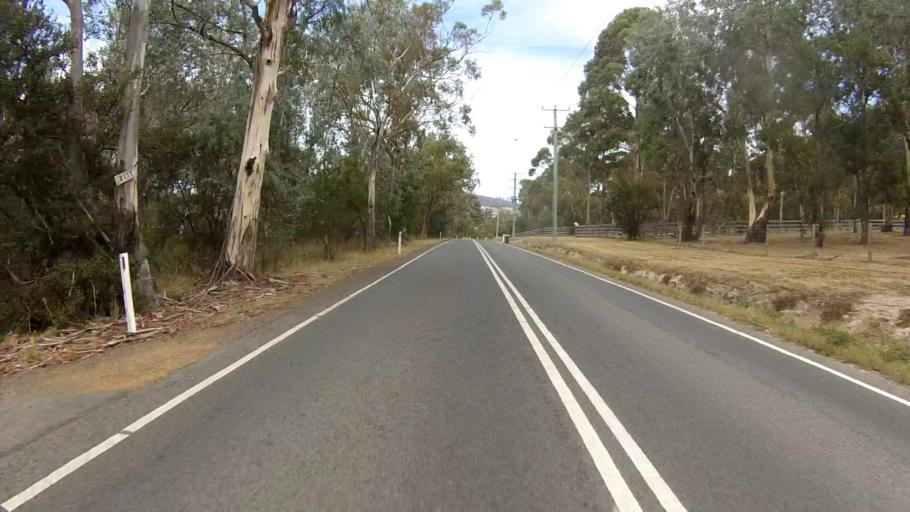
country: AU
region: Tasmania
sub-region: Clarence
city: Lauderdale
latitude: -42.8983
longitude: 147.4803
